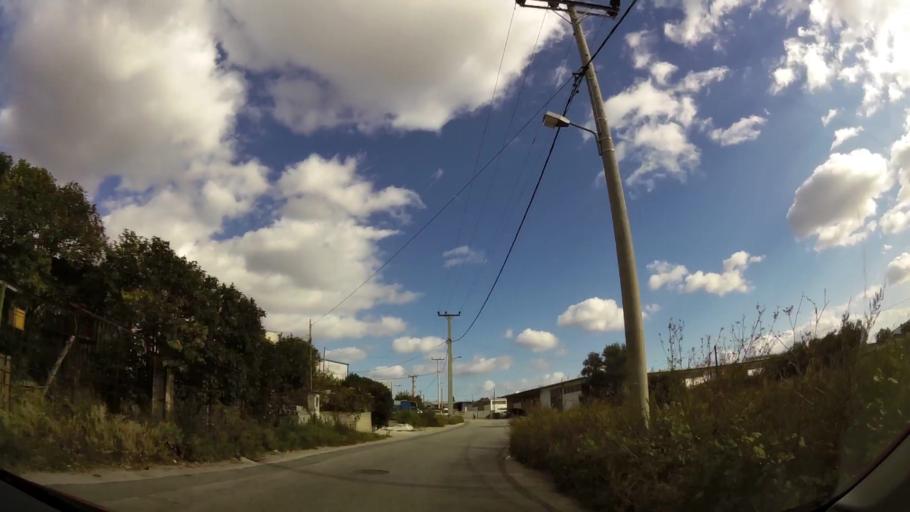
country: GR
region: Attica
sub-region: Nomarchia Anatolikis Attikis
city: Thrakomakedones
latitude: 38.1026
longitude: 23.7545
